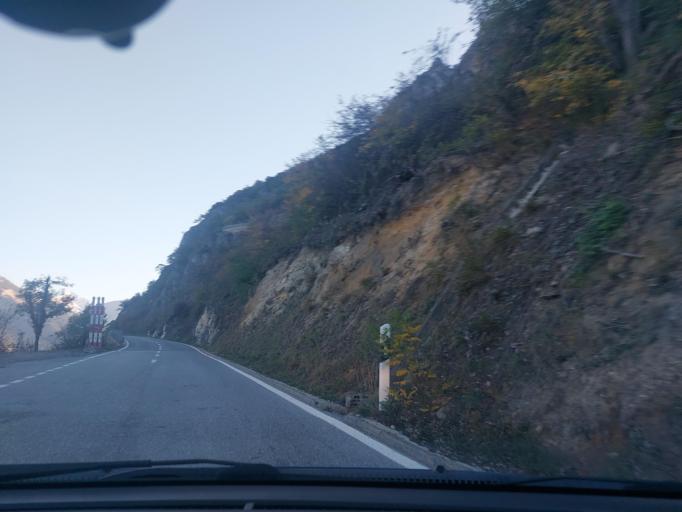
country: CH
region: Valais
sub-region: Sierre District
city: Chippis
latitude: 46.2778
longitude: 7.5478
